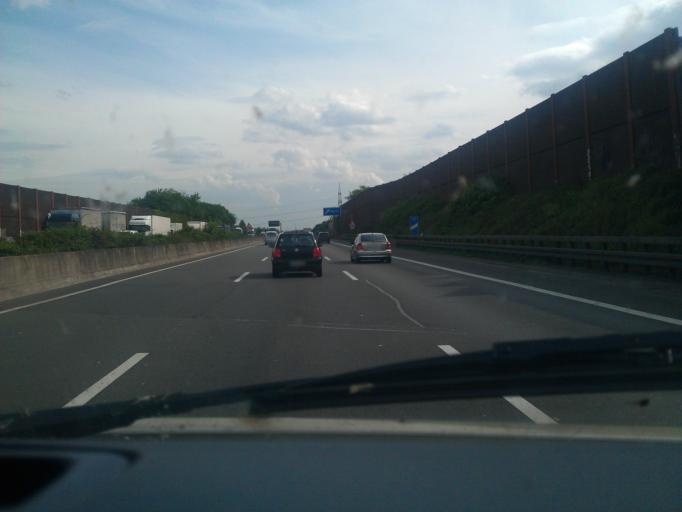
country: DE
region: North Rhine-Westphalia
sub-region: Regierungsbezirk Dusseldorf
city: Meerbusch
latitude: 51.2694
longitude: 6.6435
